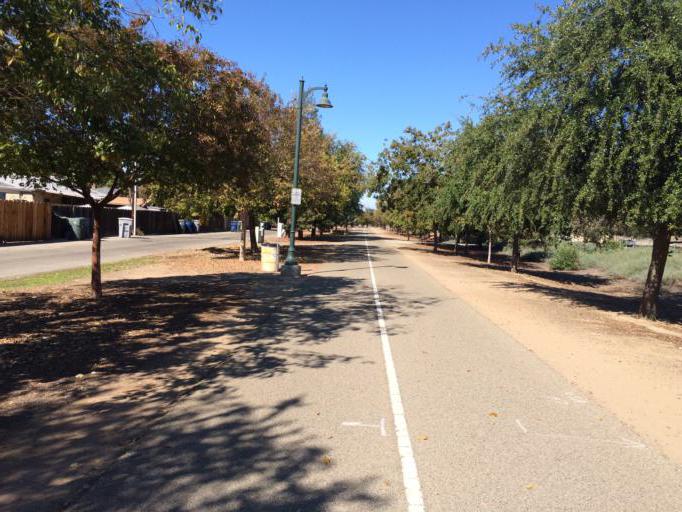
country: US
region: California
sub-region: Fresno County
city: Clovis
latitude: 36.8322
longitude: -119.7024
